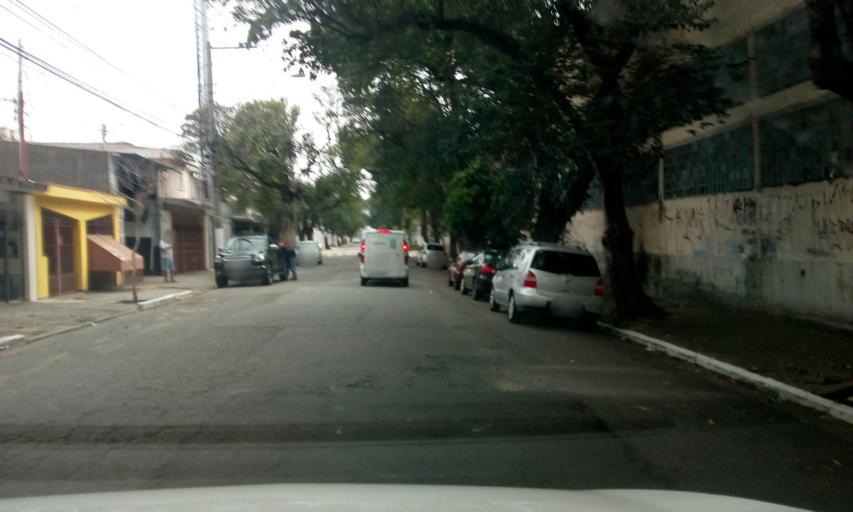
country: BR
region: Sao Paulo
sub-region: Osasco
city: Osasco
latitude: -23.5295
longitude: -46.7352
